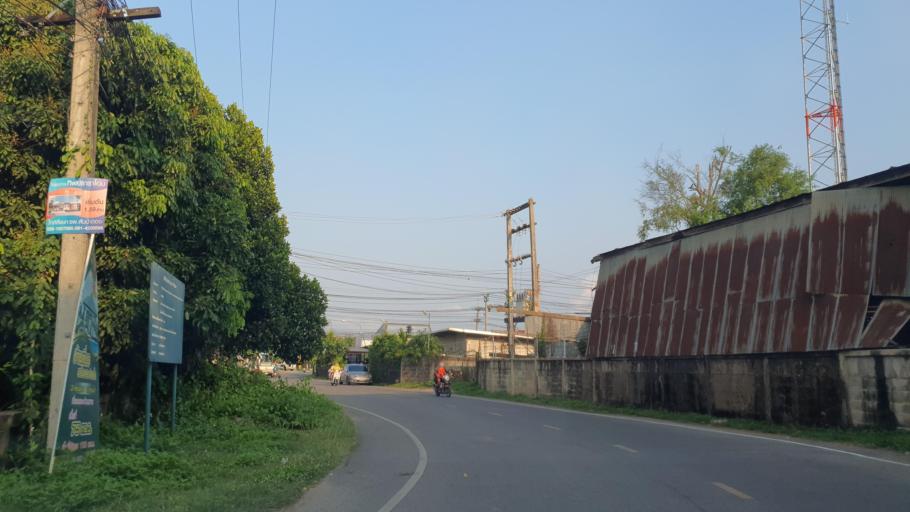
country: TH
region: Chiang Mai
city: San Pa Tong
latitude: 18.6323
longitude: 98.8966
